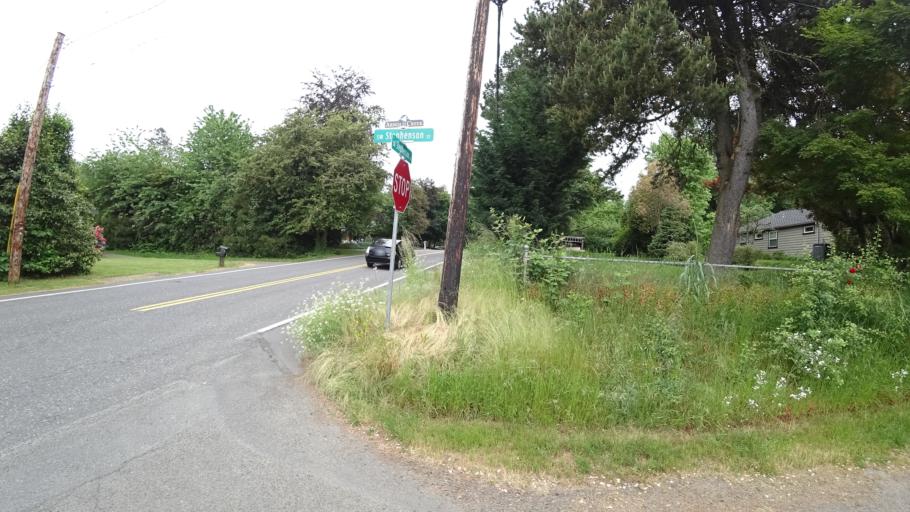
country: US
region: Oregon
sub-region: Clackamas County
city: Lake Oswego
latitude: 45.4401
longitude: -122.6907
